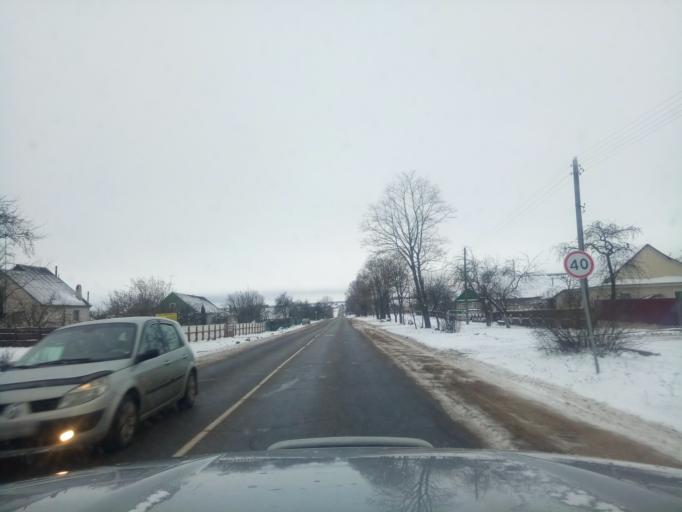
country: BY
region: Minsk
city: Kapyl'
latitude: 53.1578
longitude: 27.0989
